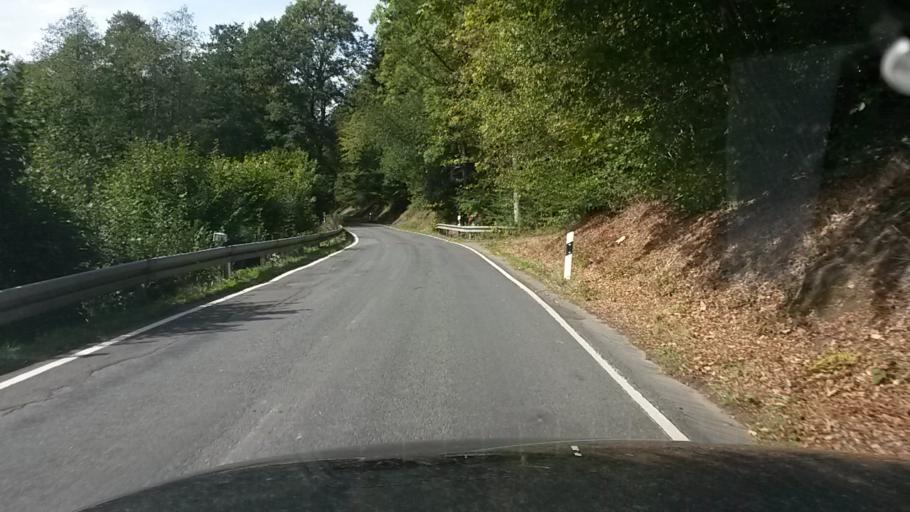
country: DE
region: North Rhine-Westphalia
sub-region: Regierungsbezirk Arnsberg
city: Luedenscheid
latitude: 51.1962
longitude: 7.6840
